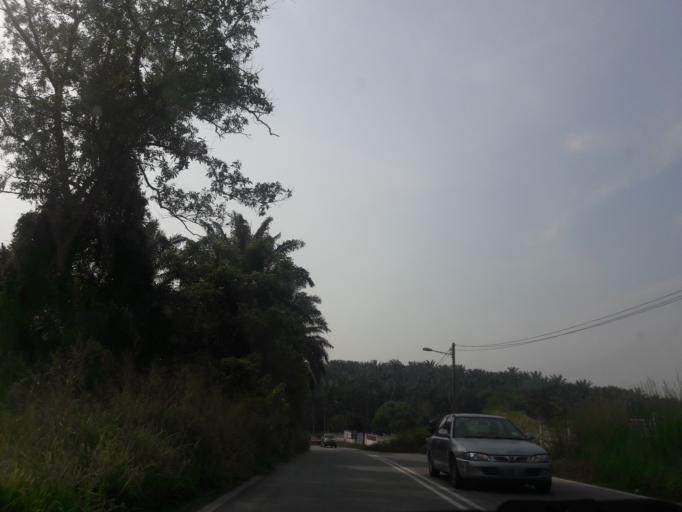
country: MY
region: Kedah
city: Kulim
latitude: 5.3706
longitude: 100.5214
